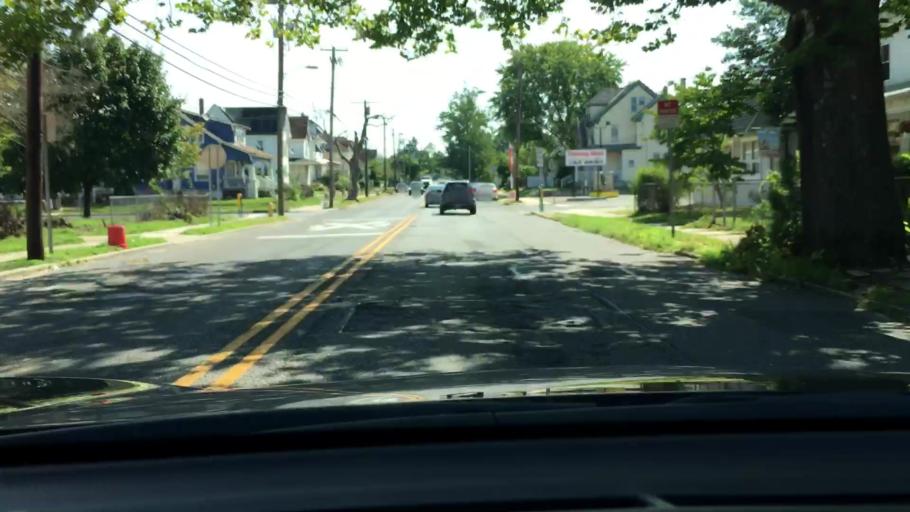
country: US
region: New Jersey
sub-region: Cumberland County
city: Millville
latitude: 39.3953
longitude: -75.0306
